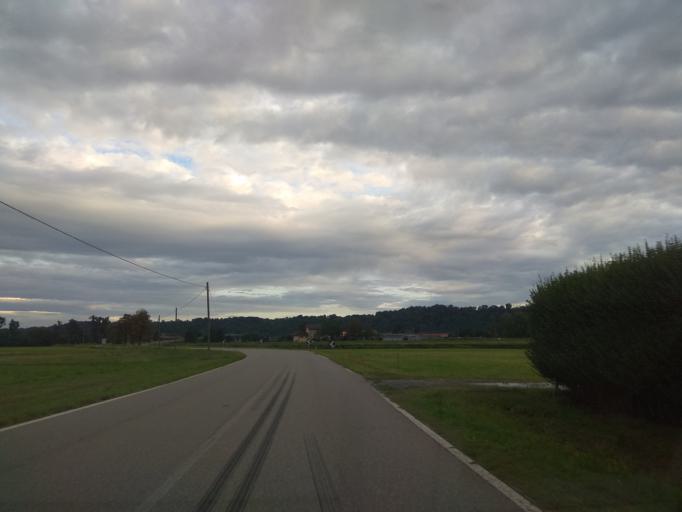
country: IT
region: Piedmont
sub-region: Provincia di Biella
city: Cerreto Castello
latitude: 45.5580
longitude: 8.1557
